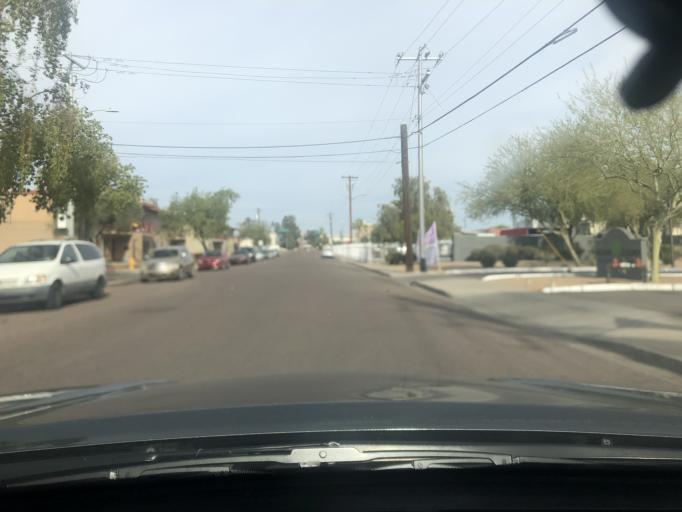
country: US
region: Arizona
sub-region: Maricopa County
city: Phoenix
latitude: 33.4496
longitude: -112.0434
